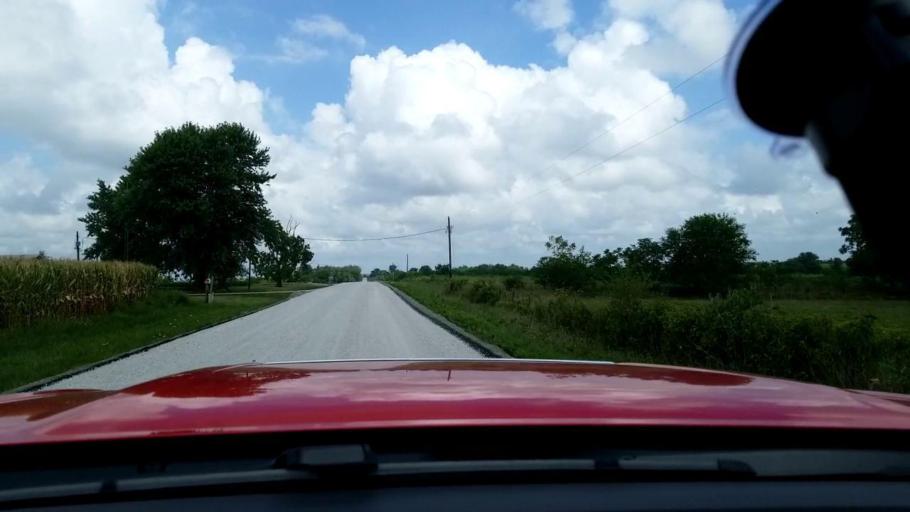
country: US
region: Iowa
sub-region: Decatur County
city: Lamoni
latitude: 40.6271
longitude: -94.0533
